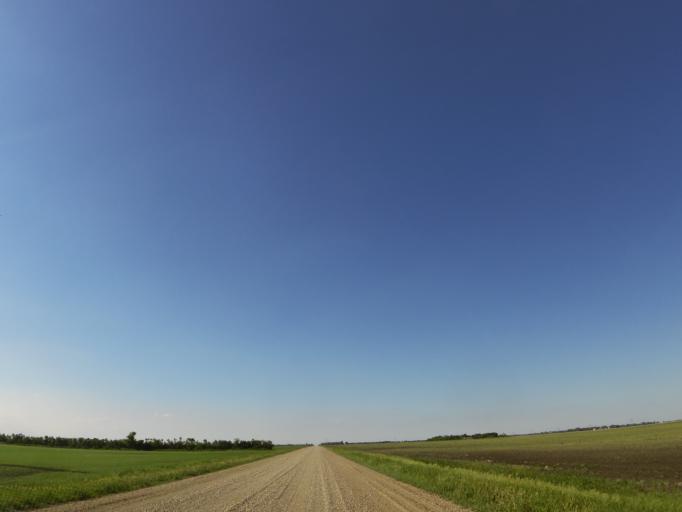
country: US
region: North Dakota
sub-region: Walsh County
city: Grafton
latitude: 48.4026
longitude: -97.2778
